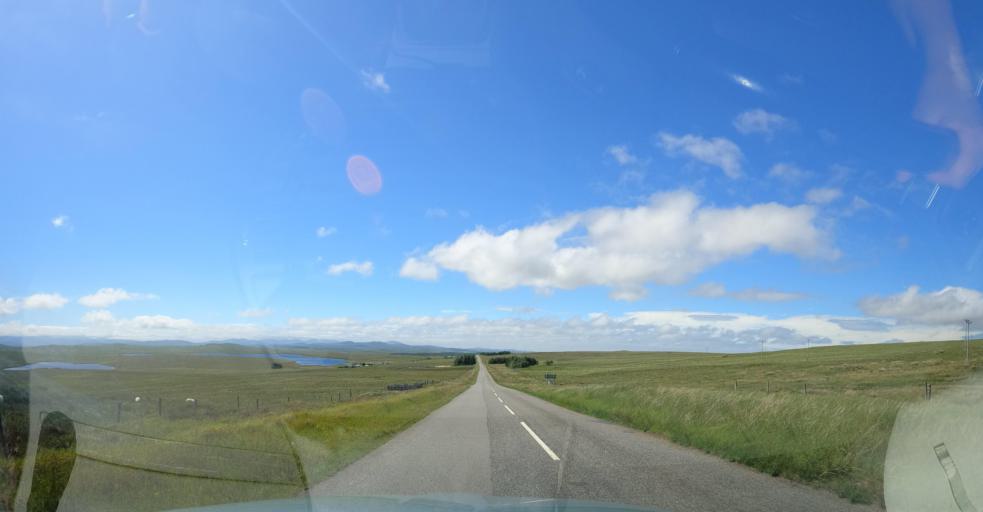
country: GB
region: Scotland
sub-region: Eilean Siar
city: Stornoway
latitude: 58.1727
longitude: -6.5913
